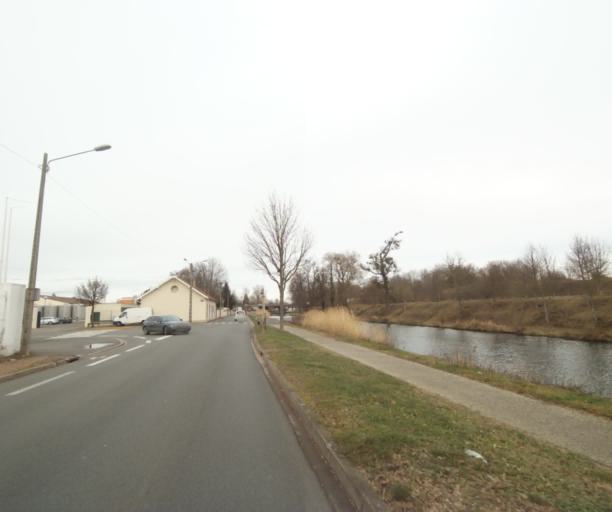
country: FR
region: Rhone-Alpes
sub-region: Departement de la Loire
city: Le Coteau
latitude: 46.0446
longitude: 4.0870
